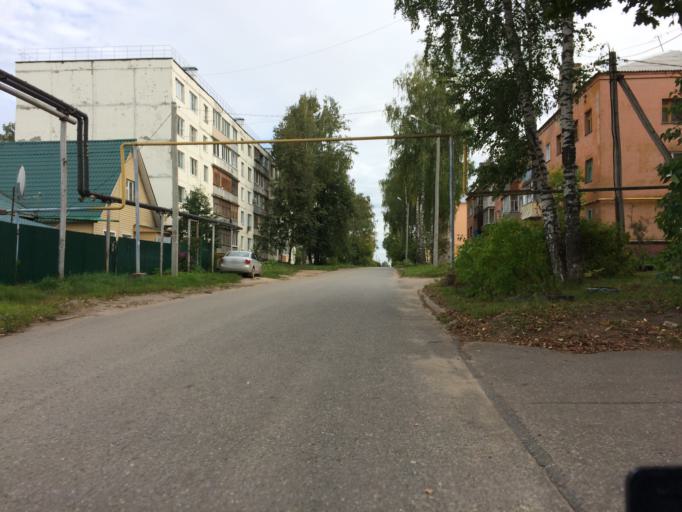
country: RU
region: Mariy-El
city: Yoshkar-Ola
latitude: 56.6580
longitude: 47.9790
